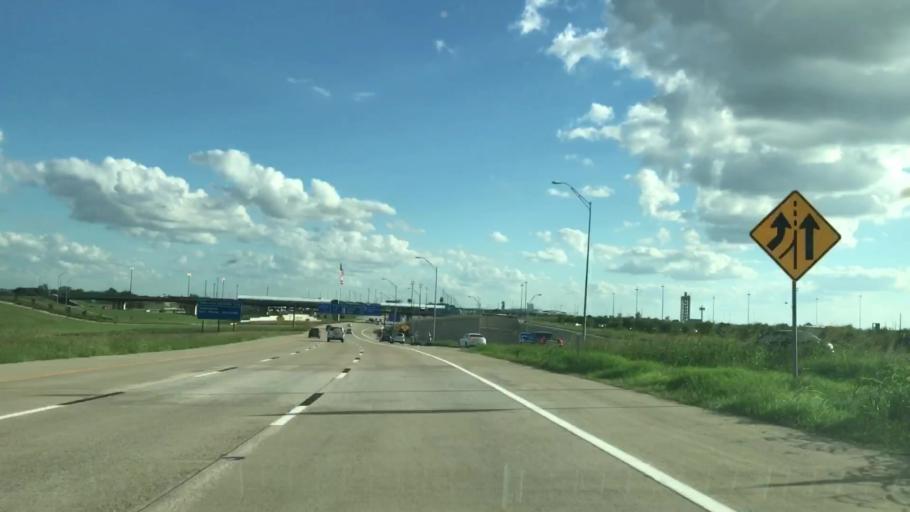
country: US
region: Texas
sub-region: Dallas County
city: Coppell
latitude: 32.9305
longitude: -97.0414
